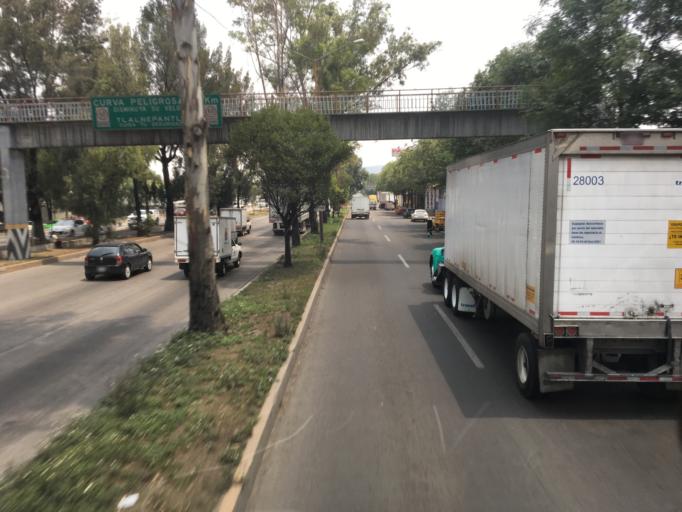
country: MX
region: Mexico
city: Tlalnepantla
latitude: 19.5390
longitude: -99.1815
